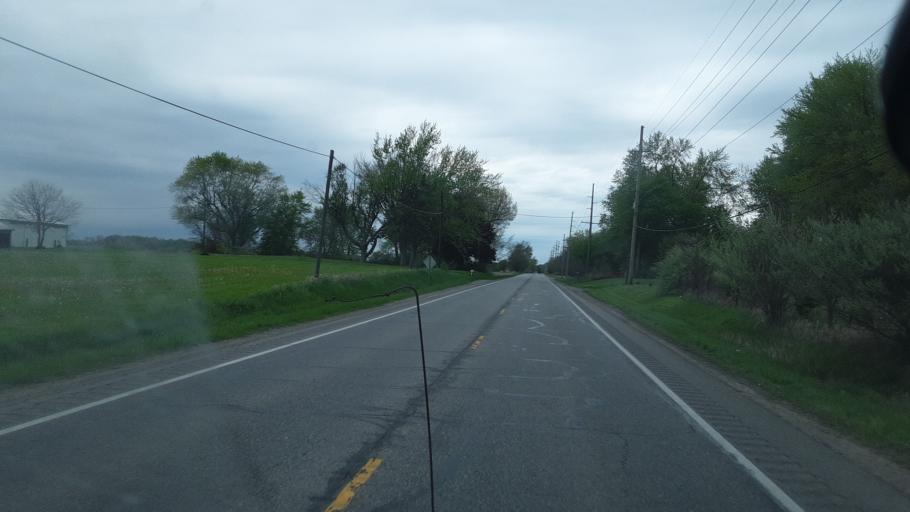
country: US
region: Indiana
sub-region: Elkhart County
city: Goshen
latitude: 41.6144
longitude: -85.8303
